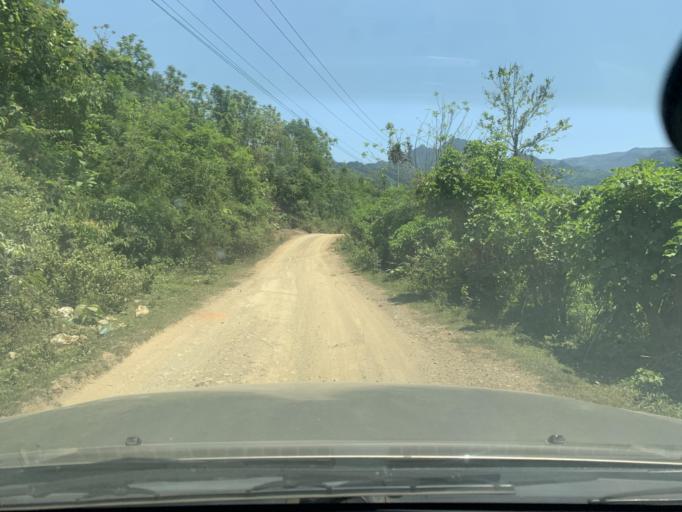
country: LA
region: Louangphabang
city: Louangphabang
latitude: 19.9043
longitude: 102.2513
